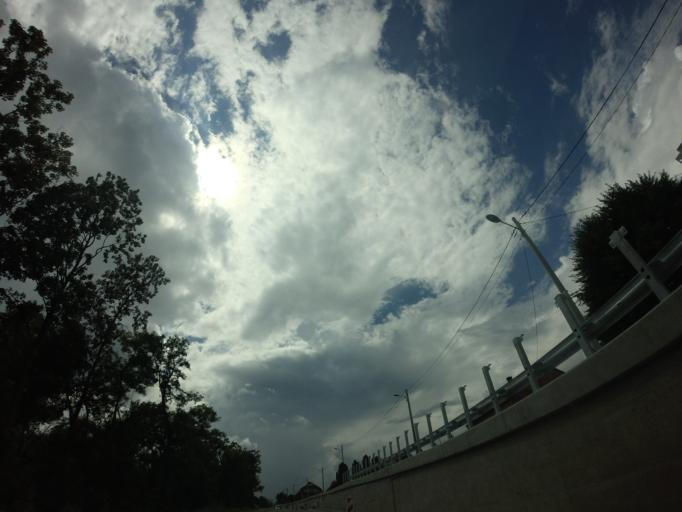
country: PL
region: Swietokrzyskie
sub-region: Powiat opatowski
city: Tarlow
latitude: 51.0410
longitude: 21.6976
